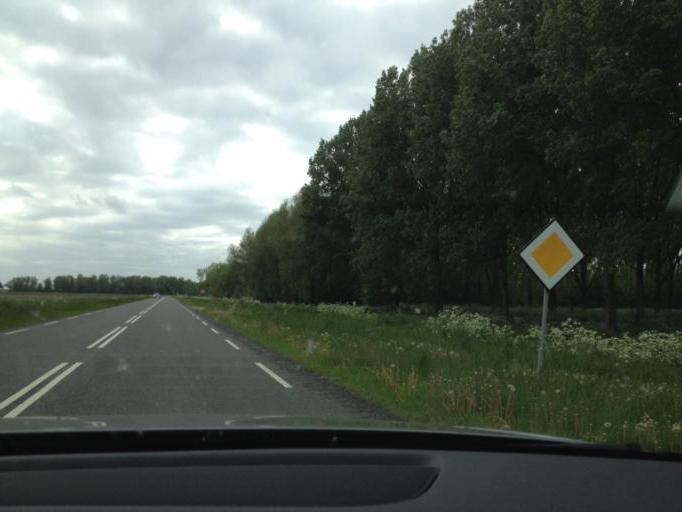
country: NL
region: Utrecht
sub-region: Gemeente Bunschoten
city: Spakenburg
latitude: 52.3055
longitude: 5.3350
